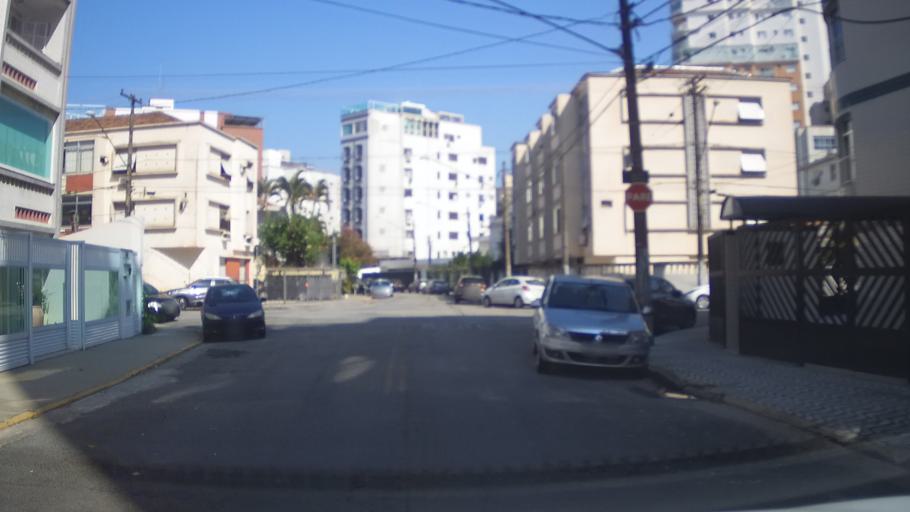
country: BR
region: Sao Paulo
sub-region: Santos
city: Santos
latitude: -23.9889
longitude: -46.3036
